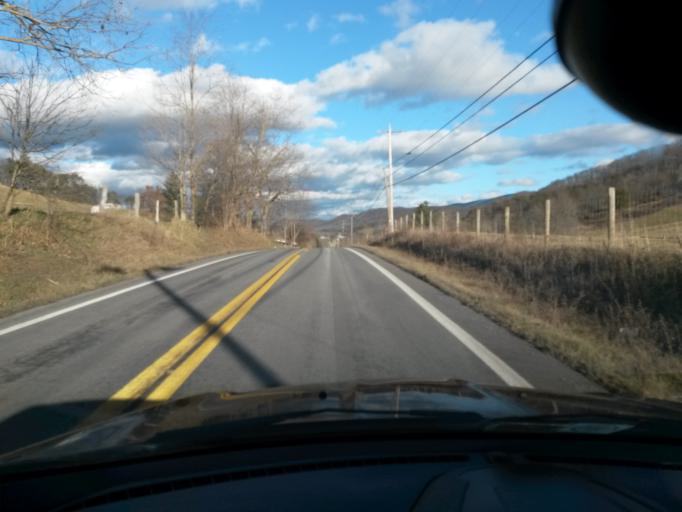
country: US
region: Virginia
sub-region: Giles County
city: Pearisburg
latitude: 37.4265
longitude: -80.7258
